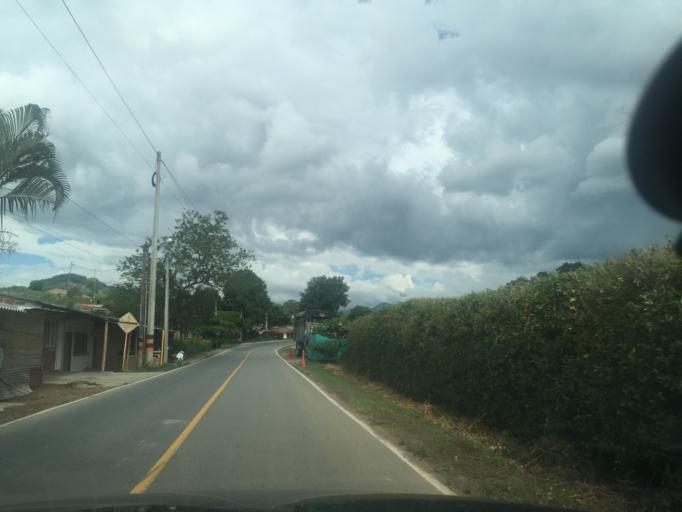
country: CO
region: Valle del Cauca
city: Caicedonia
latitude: 4.3425
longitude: -75.8524
